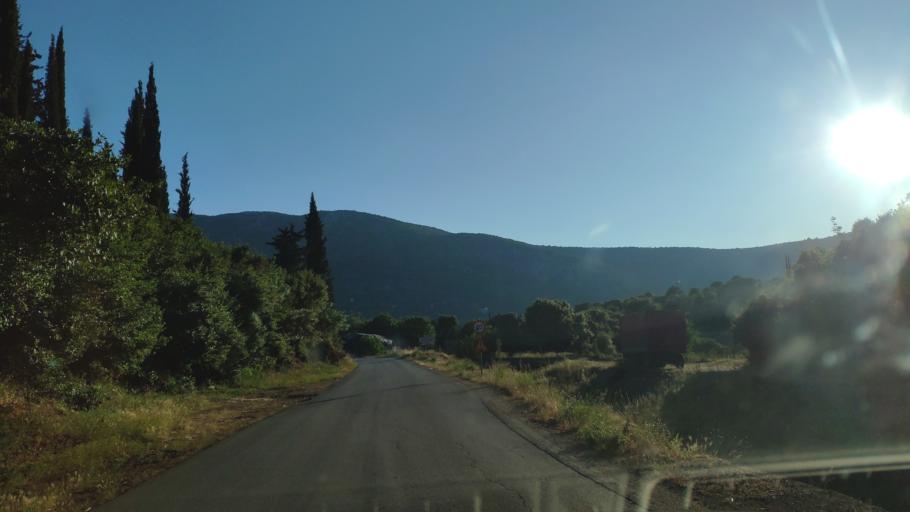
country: GR
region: West Greece
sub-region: Nomos Aitolias kai Akarnanias
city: Astakos
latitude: 38.5976
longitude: 21.0939
